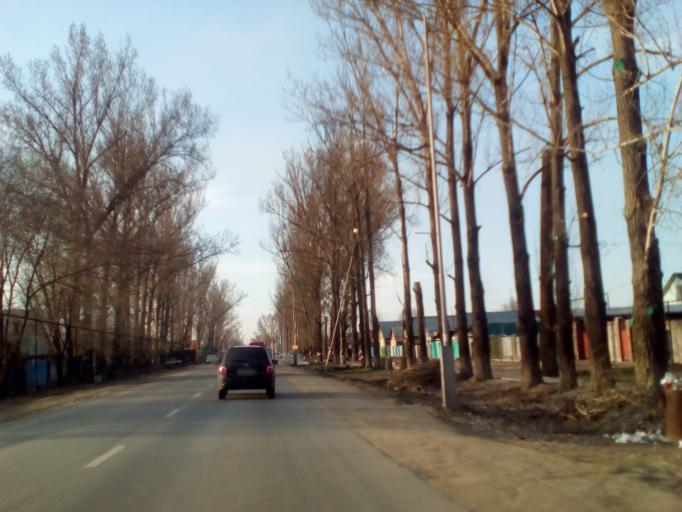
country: KZ
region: Almaty Oblysy
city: Burunday
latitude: 43.2568
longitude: 76.7808
